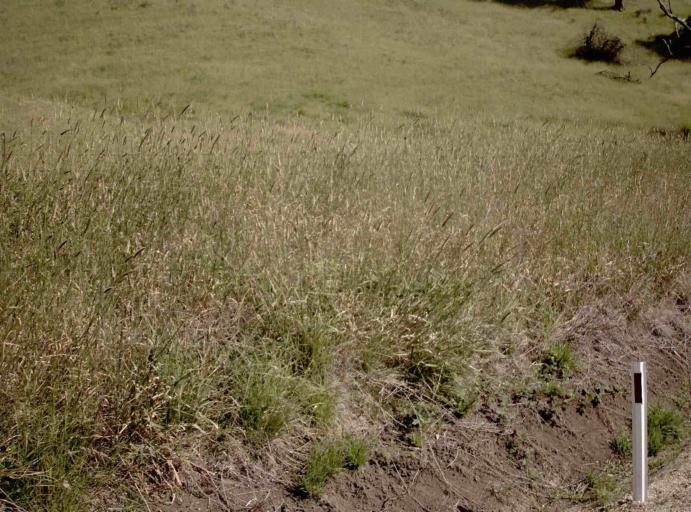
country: AU
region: Victoria
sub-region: East Gippsland
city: Lakes Entrance
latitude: -37.5116
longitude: 148.1679
